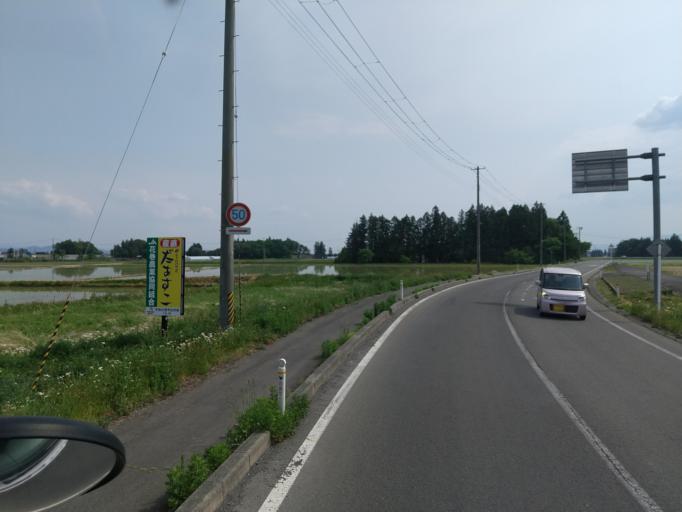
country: JP
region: Iwate
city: Hanamaki
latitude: 39.4017
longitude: 141.0898
